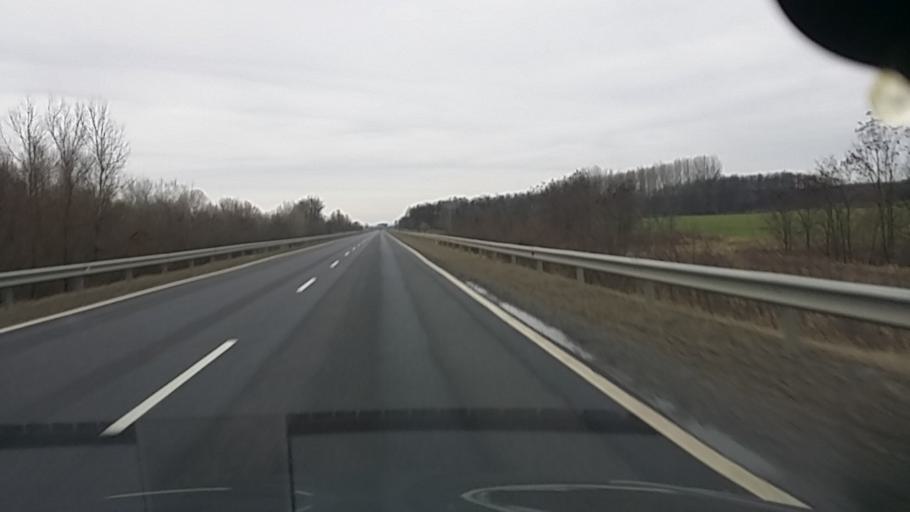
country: HU
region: Szabolcs-Szatmar-Bereg
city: Nagykallo
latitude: 47.9123
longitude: 21.8185
